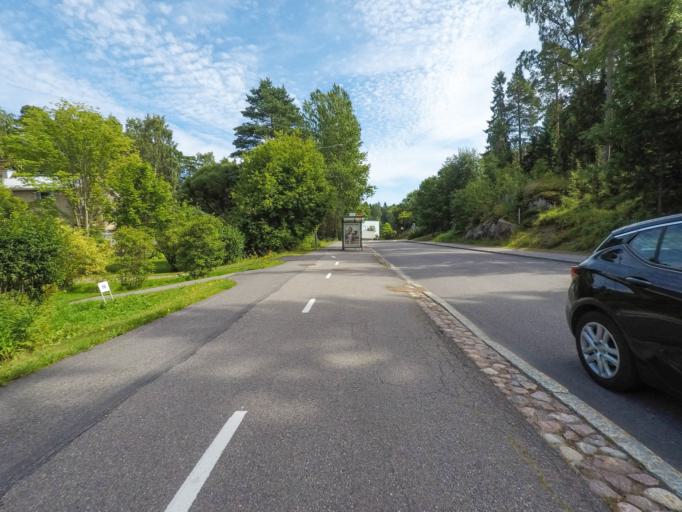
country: FI
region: Uusimaa
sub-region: Helsinki
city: Vantaa
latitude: 60.1661
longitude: 25.0790
